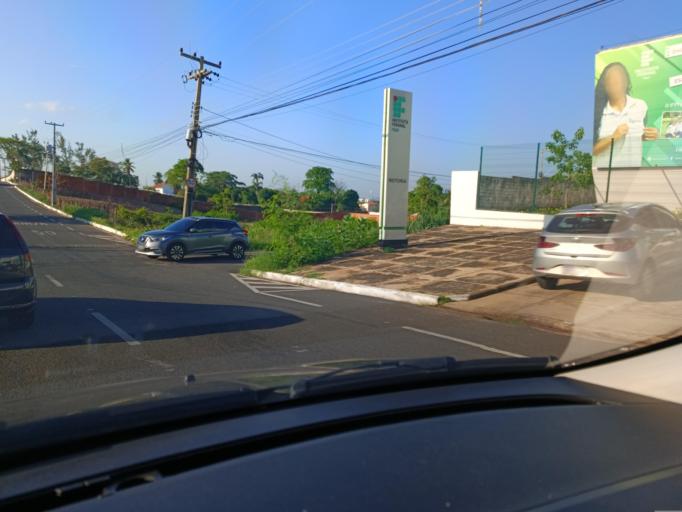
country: BR
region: Piaui
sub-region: Teresina
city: Teresina
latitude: -5.0762
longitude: -42.7516
